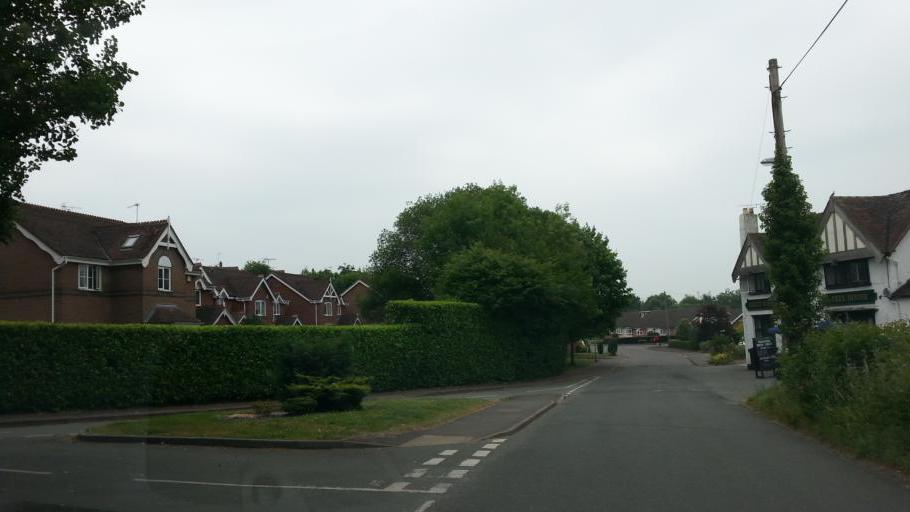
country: GB
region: England
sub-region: Staffordshire
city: Colwich
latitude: 52.8328
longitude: -1.9926
